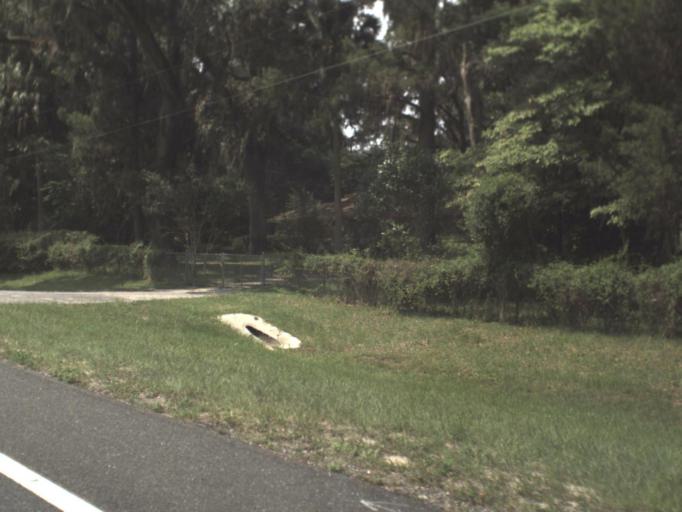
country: US
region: Florida
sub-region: Levy County
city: Chiefland
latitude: 29.4479
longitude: -82.8424
